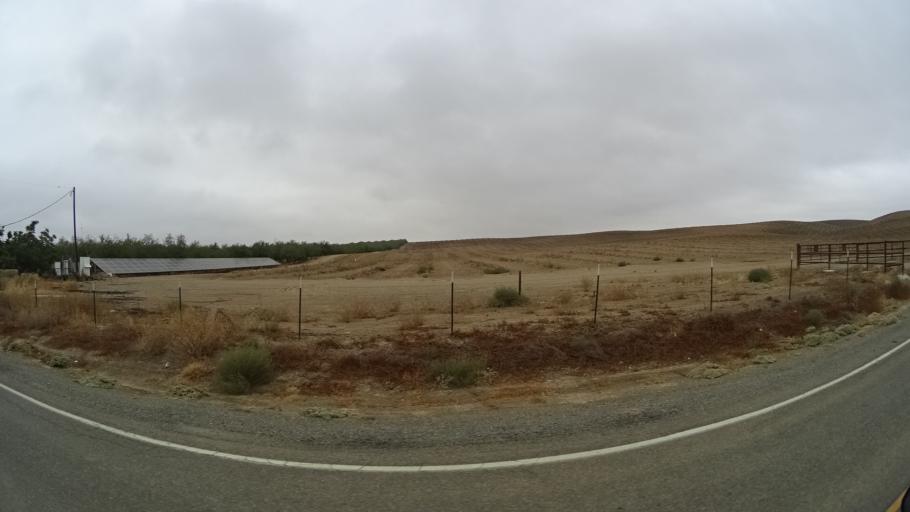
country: US
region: California
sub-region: Yolo County
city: Dunnigan
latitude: 38.8819
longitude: -121.9900
